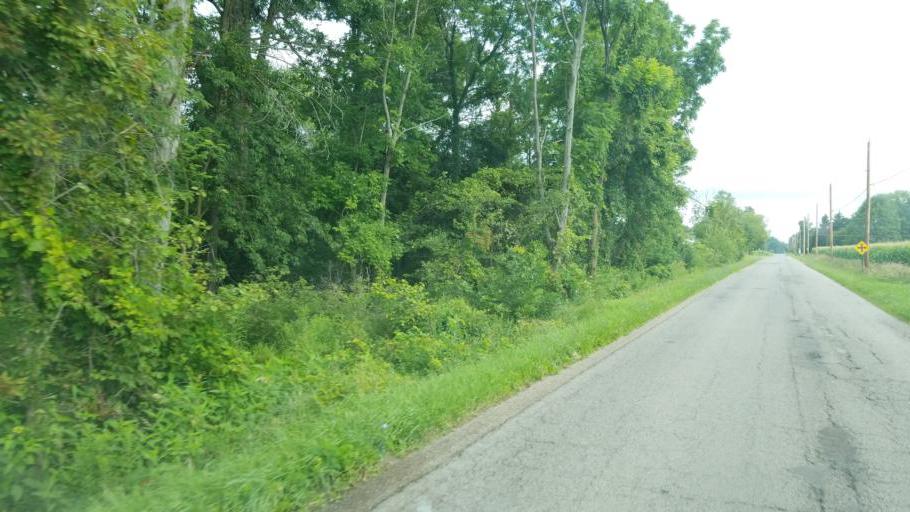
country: US
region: Ohio
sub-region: Crawford County
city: Galion
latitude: 40.6952
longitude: -82.7839
